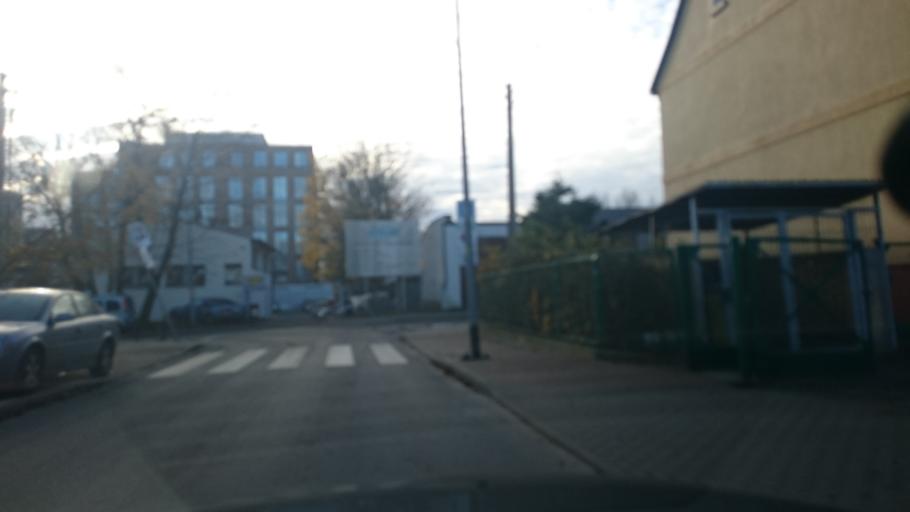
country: PL
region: Pomeranian Voivodeship
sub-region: Sopot
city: Sopot
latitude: 54.4064
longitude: 18.5752
